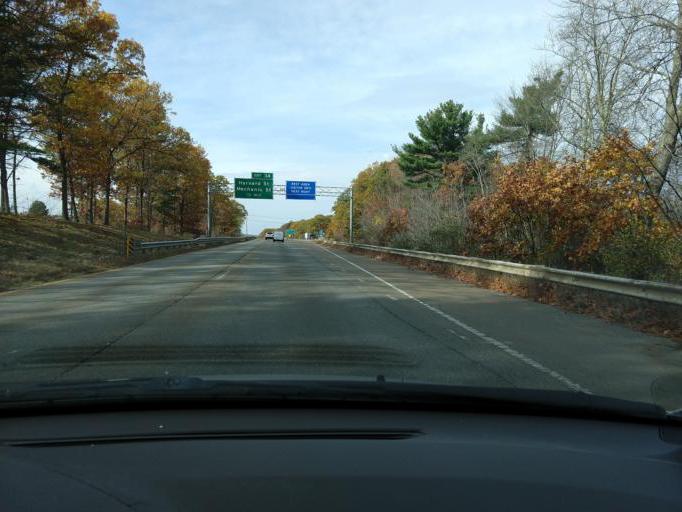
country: US
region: Massachusetts
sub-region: Middlesex County
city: Shirley
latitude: 42.5207
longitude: -71.6979
